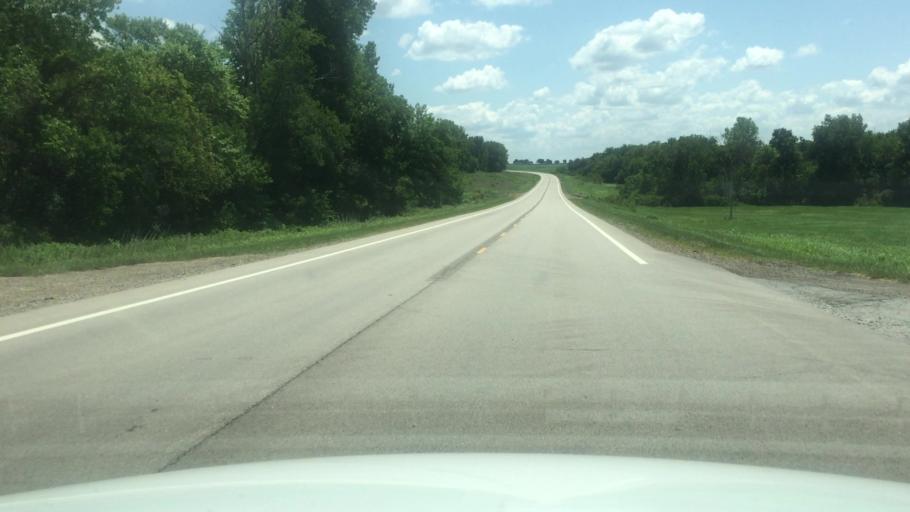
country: US
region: Kansas
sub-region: Brown County
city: Horton
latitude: 39.6238
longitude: -95.3501
